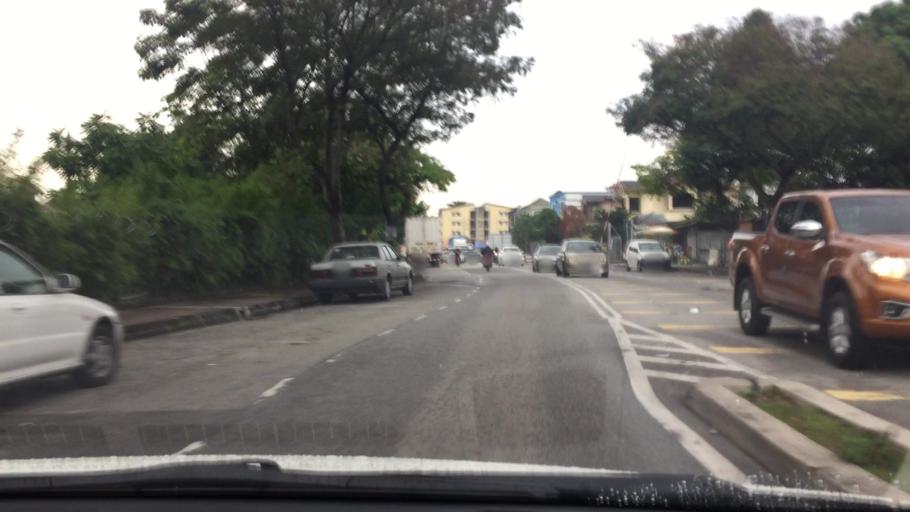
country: MY
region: Selangor
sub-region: Petaling
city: Petaling Jaya
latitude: 3.0767
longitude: 101.6441
